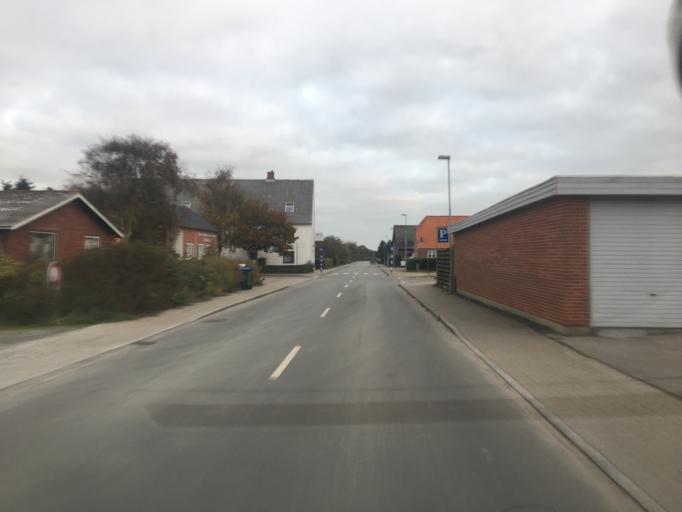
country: DE
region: Schleswig-Holstein
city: Rodenas
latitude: 54.9641
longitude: 8.6971
